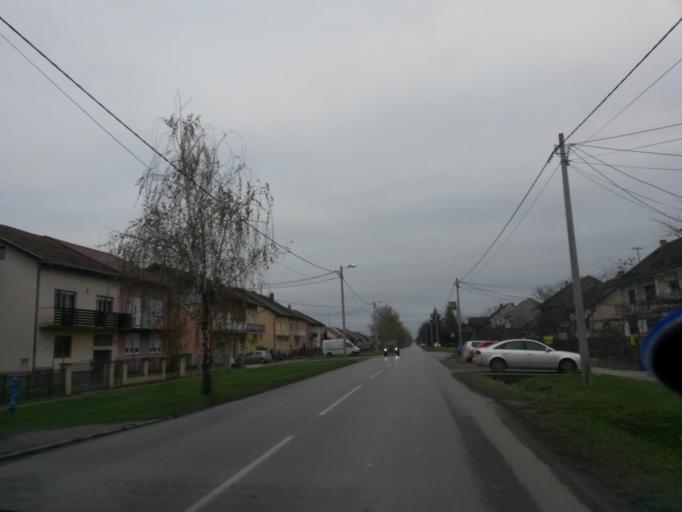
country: HR
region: Osjecko-Baranjska
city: Tenja
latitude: 45.5084
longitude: 18.7384
